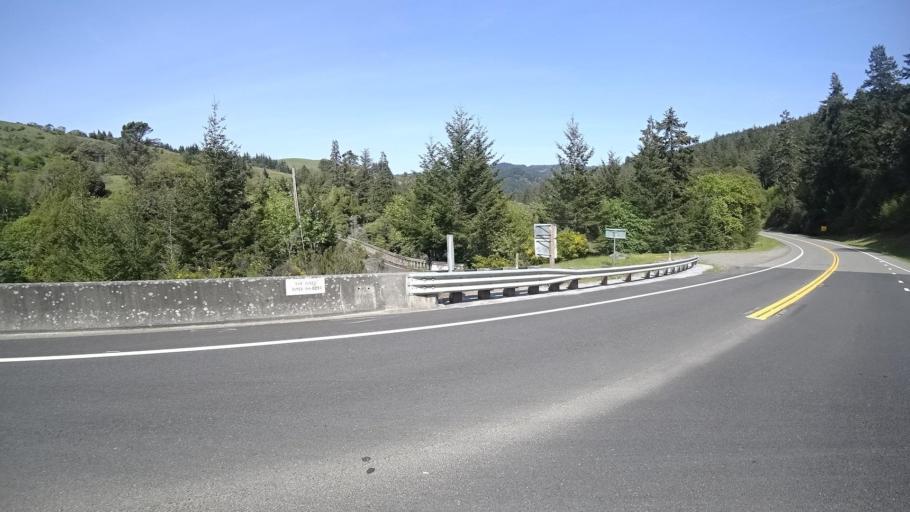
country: US
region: California
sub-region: Humboldt County
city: Hydesville
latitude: 40.4685
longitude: -123.7993
